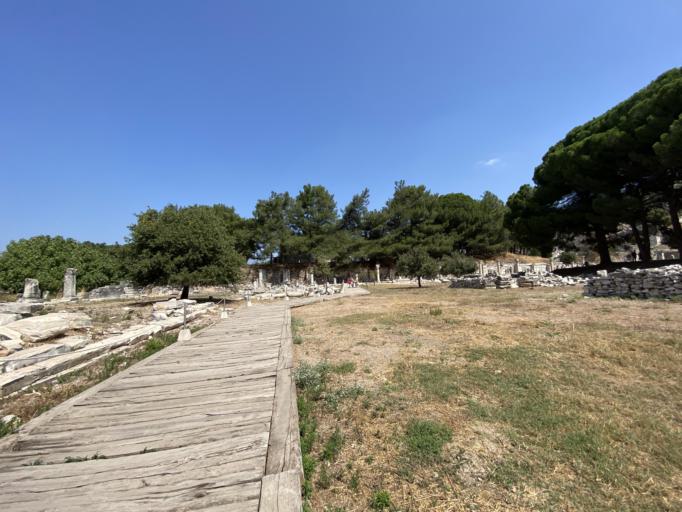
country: TR
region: Izmir
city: Selcuk
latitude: 37.9402
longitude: 27.3401
